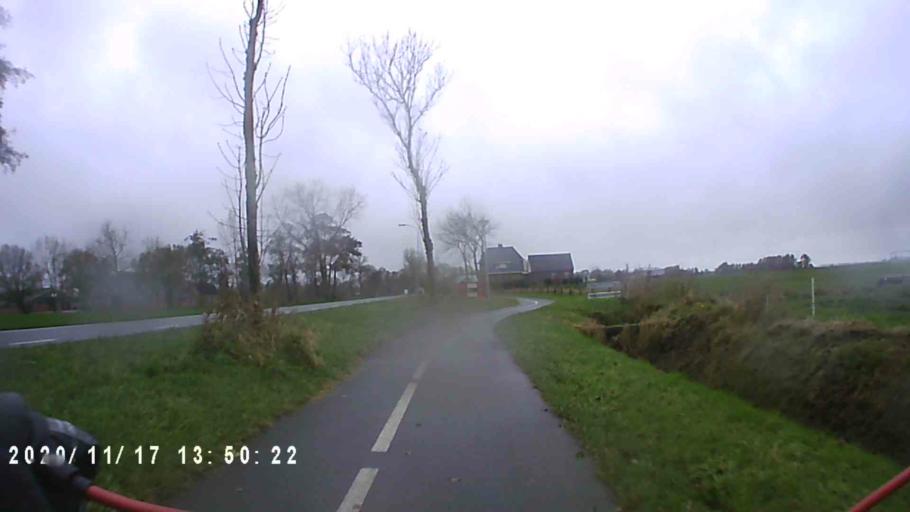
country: NL
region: Groningen
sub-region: Gemeente Zuidhorn
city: Zuidhorn
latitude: 53.2302
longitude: 6.3671
